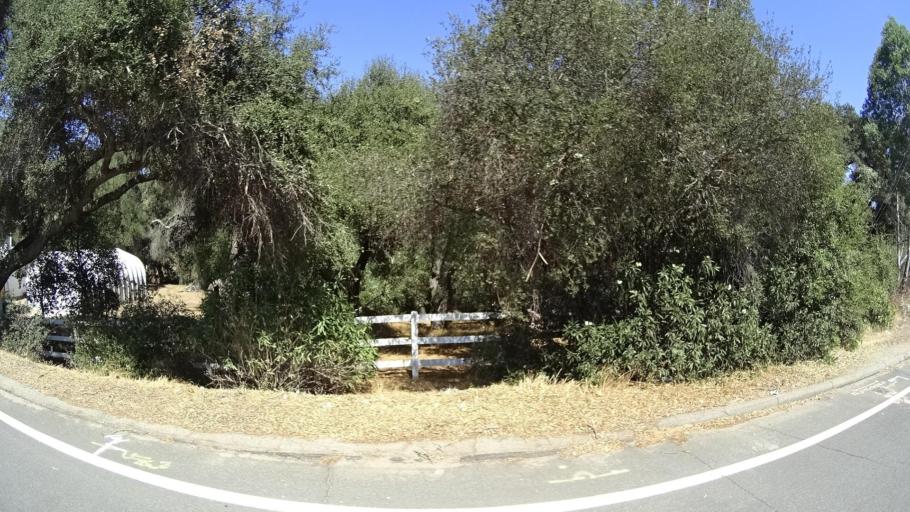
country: US
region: California
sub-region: San Diego County
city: Hidden Meadows
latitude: 33.2579
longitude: -117.0706
